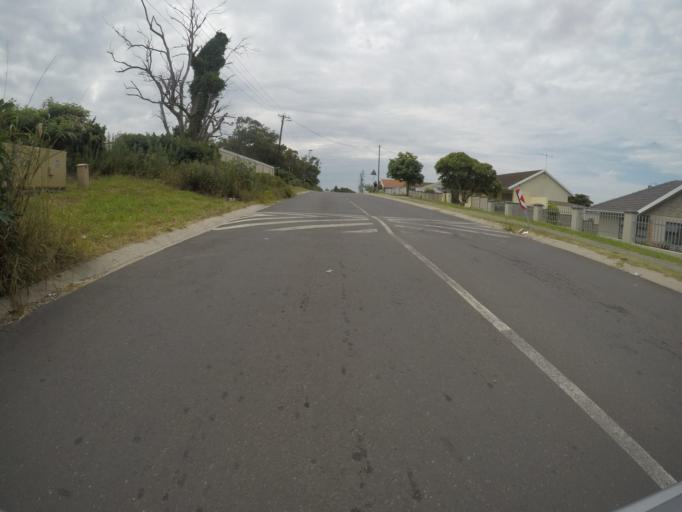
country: ZA
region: Eastern Cape
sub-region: Buffalo City Metropolitan Municipality
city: East London
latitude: -32.9933
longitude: 27.8694
